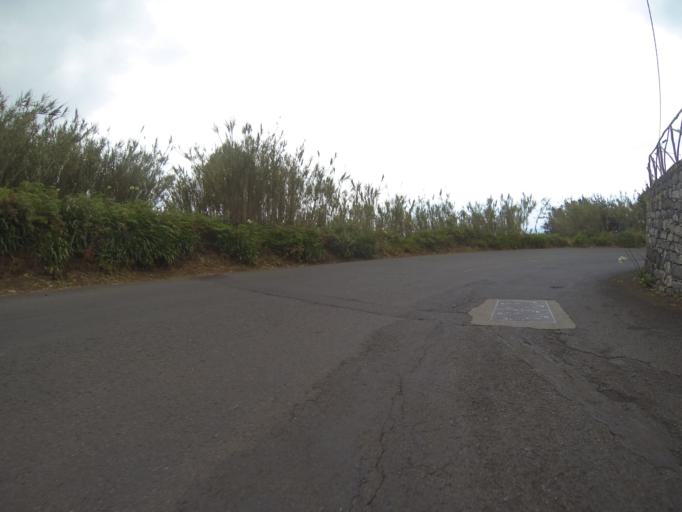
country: PT
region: Madeira
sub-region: Porto Moniz
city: Porto Moniz
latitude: 32.8605
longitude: -17.1723
